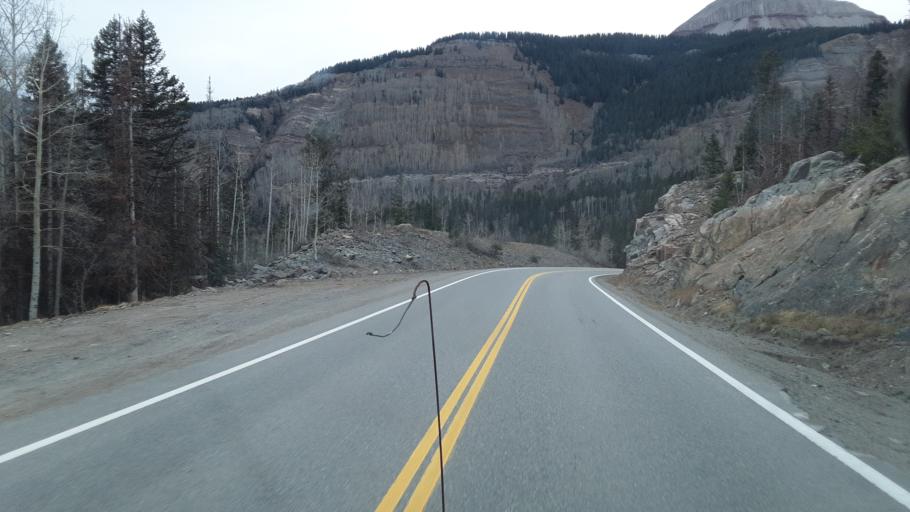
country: US
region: Colorado
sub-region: San Juan County
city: Silverton
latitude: 37.6776
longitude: -107.7829
